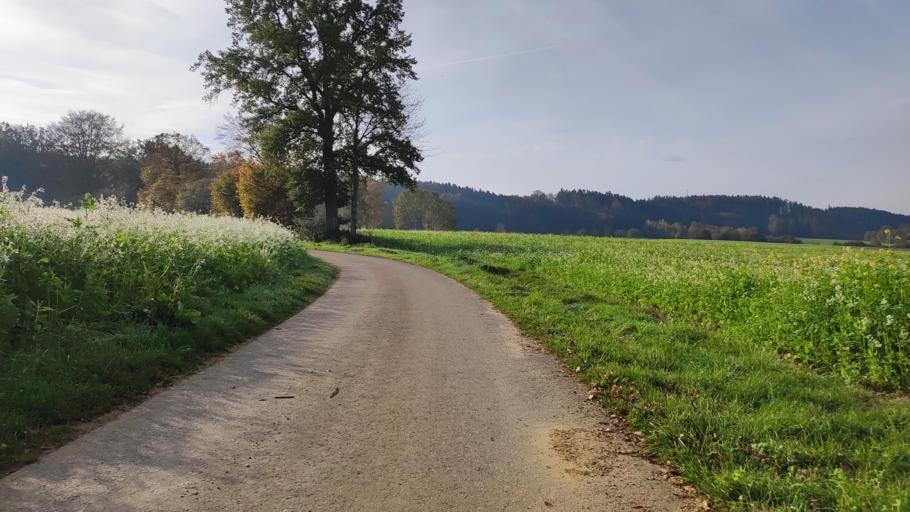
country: DE
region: Bavaria
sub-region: Swabia
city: Ziemetshausen
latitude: 48.2992
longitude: 10.5712
